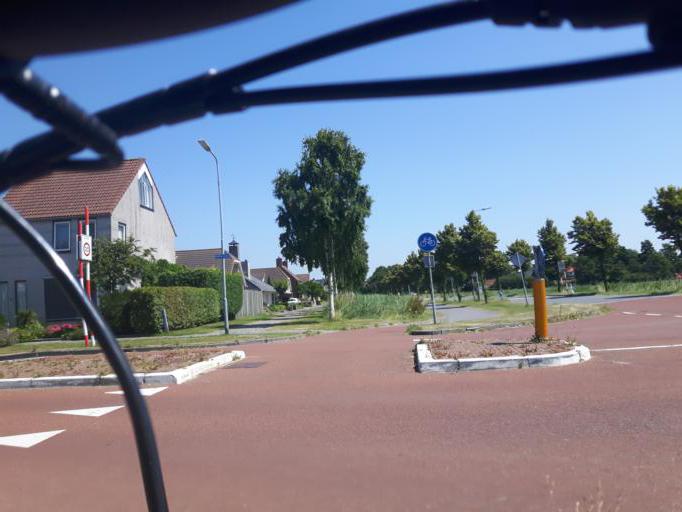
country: NL
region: Zeeland
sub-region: Gemeente Veere
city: Veere
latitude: 51.5032
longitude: 3.6659
